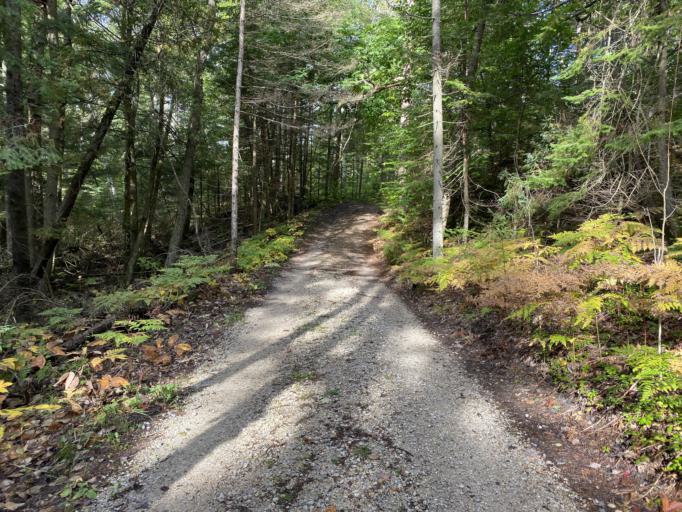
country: US
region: Michigan
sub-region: Mackinac County
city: Saint Ignace
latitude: 45.7476
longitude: -84.8790
